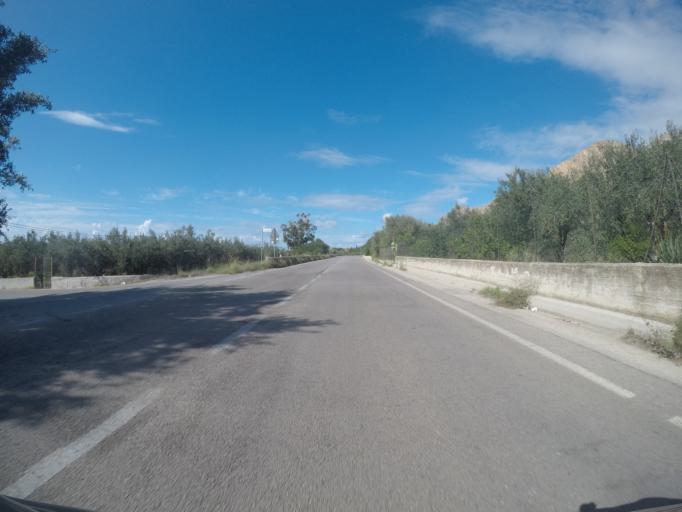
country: IT
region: Sicily
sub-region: Palermo
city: Agliandroni-Paternella
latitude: 38.1174
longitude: 13.0763
